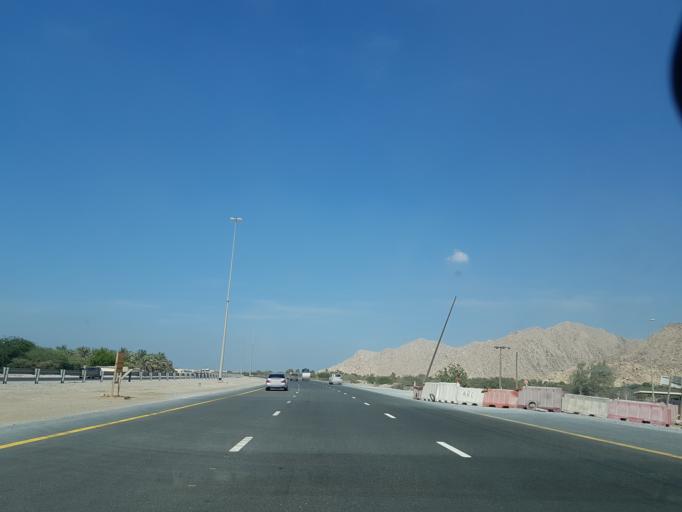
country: AE
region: Ra's al Khaymah
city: Ras al-Khaimah
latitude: 25.8075
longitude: 56.0302
